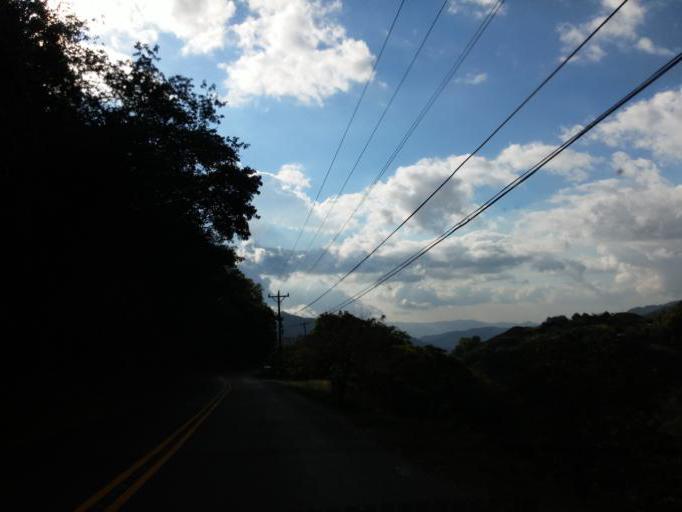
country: CR
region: San Jose
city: San Ignacio
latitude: 9.7969
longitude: -84.1362
